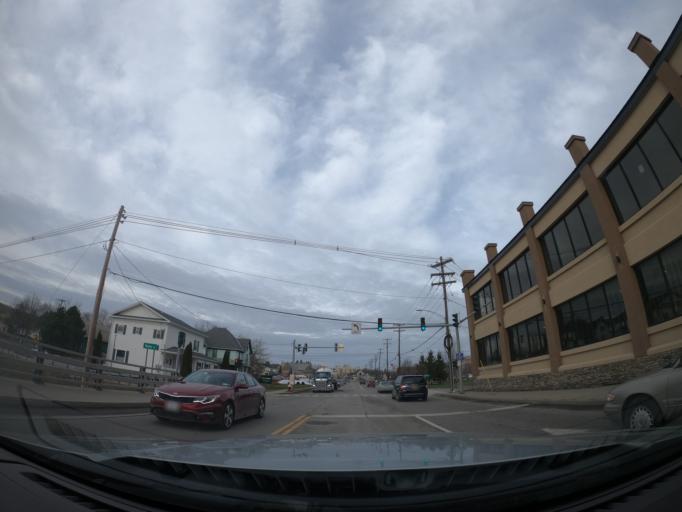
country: US
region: New York
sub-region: Yates County
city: Penn Yan
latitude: 42.6582
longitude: -77.0555
